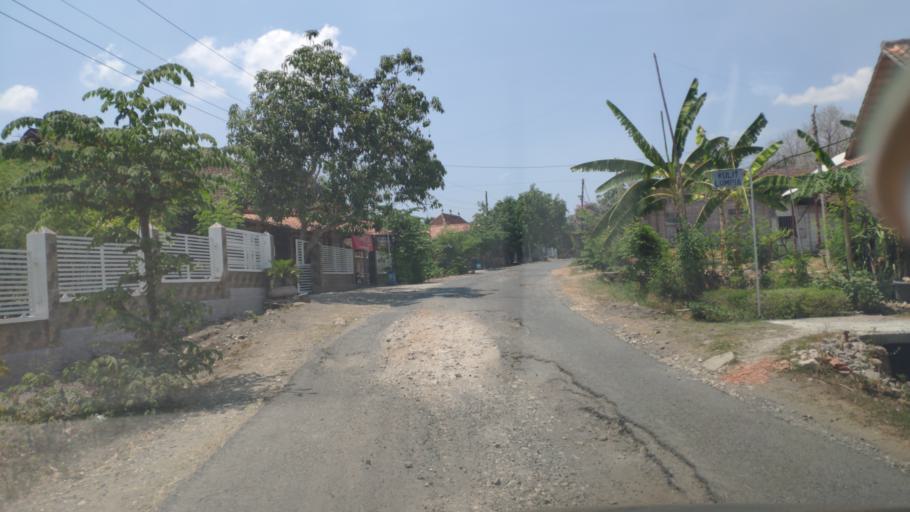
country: ID
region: Central Java
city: Randublatung
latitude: -7.2149
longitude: 111.3924
